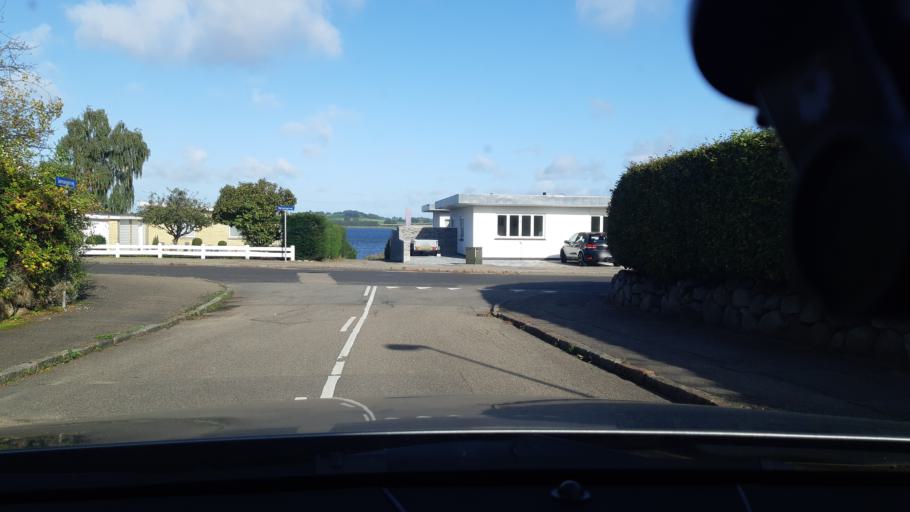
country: DK
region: Zealand
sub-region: Holbaek Kommune
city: Holbaek
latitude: 55.7171
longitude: 11.6848
